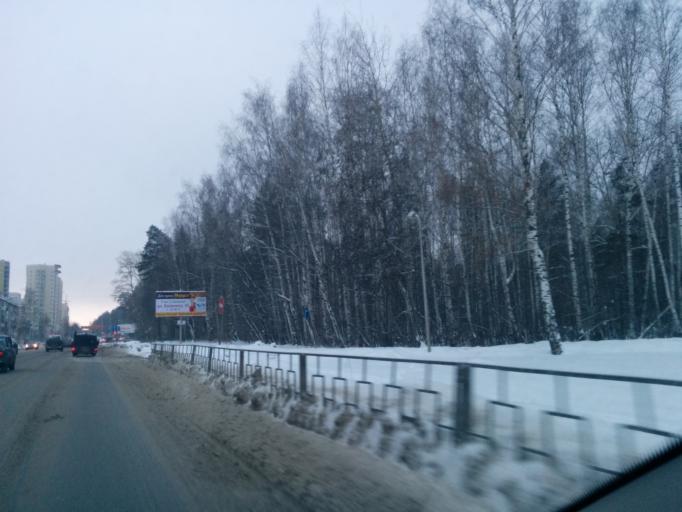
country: RU
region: Perm
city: Kondratovo
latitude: 58.0380
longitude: 56.0234
